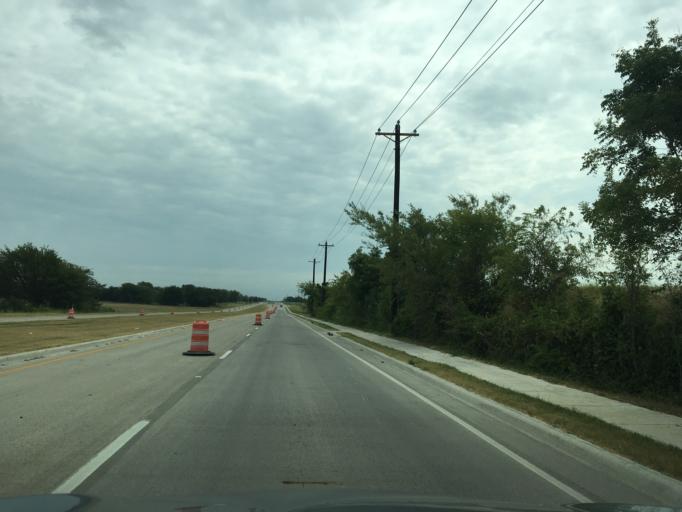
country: US
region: Texas
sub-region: Collin County
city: Anna
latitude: 33.3049
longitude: -96.5249
